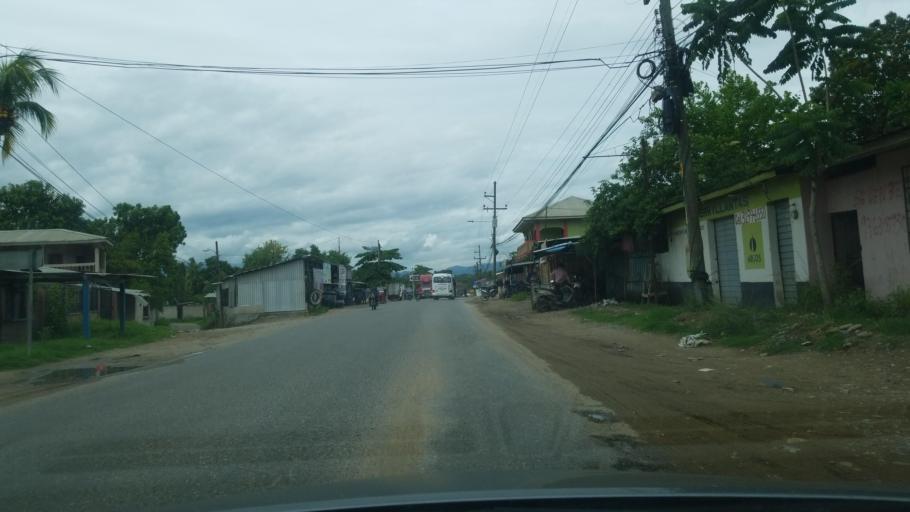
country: HN
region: Santa Barbara
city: La Flecha
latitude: 15.2952
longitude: -88.4880
